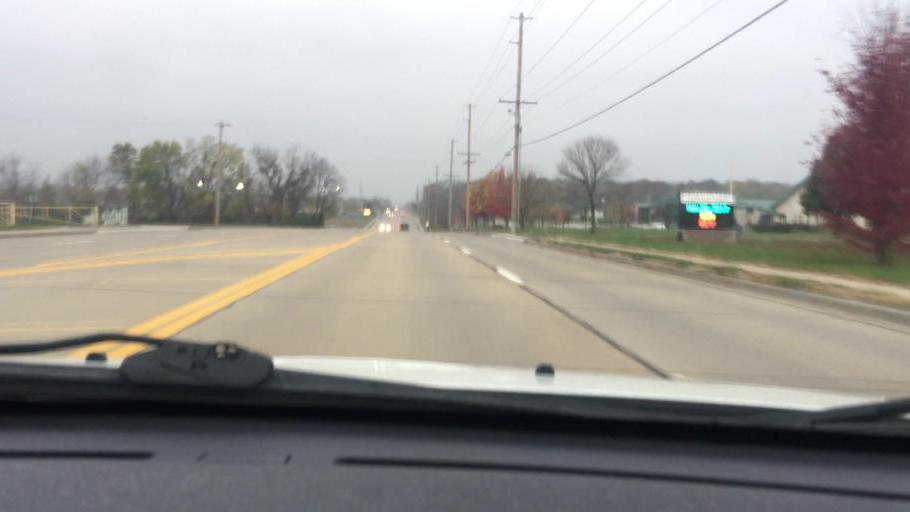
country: US
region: Missouri
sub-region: Saint Charles County
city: O'Fallon
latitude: 38.8215
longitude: -90.6692
